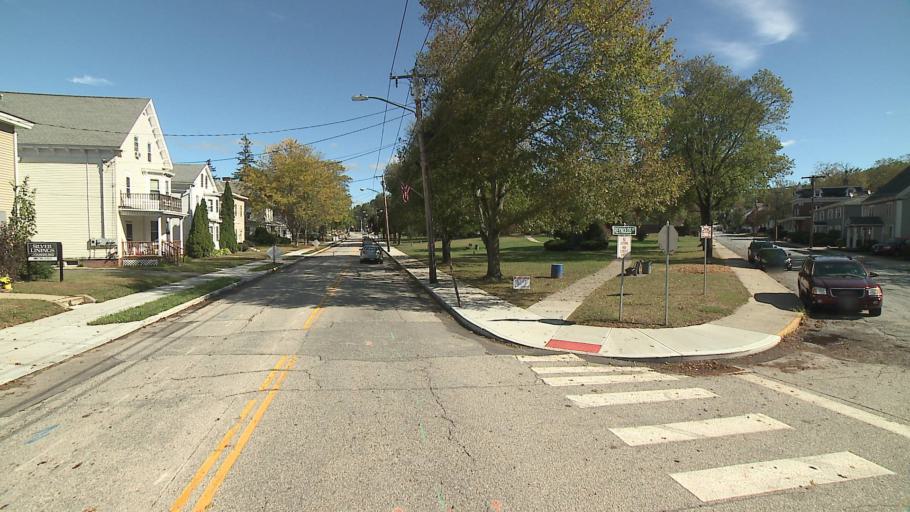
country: US
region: Connecticut
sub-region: Windham County
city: Danielson
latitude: 41.8071
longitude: -71.8815
